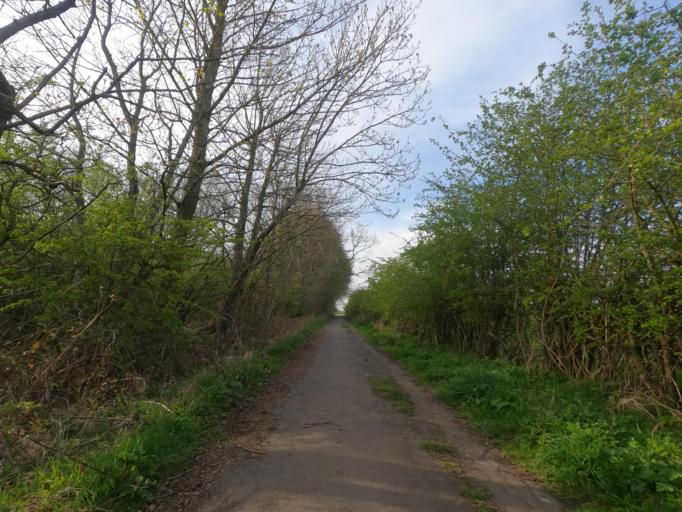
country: GB
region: England
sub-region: Northumberland
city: Cramlington
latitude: 55.0755
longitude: -1.6060
